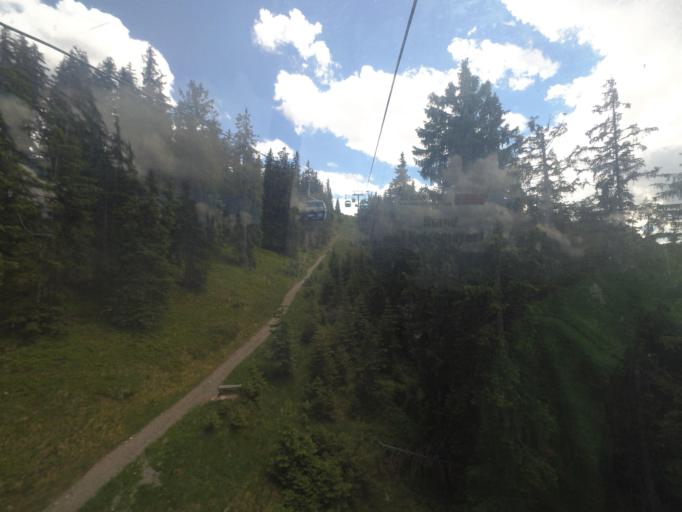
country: AT
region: Salzburg
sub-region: Politischer Bezirk Zell am See
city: Viehhofen
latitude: 47.4142
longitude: 12.7144
